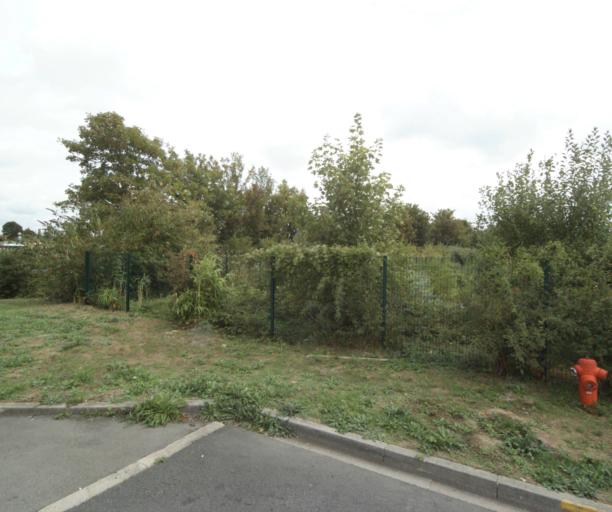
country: FR
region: Nord-Pas-de-Calais
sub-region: Departement du Nord
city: Lesquin
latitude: 50.5819
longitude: 3.1241
